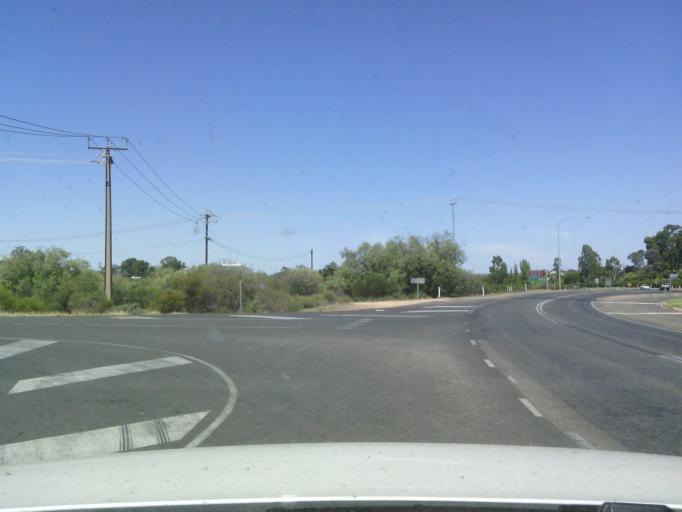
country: AU
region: South Australia
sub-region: Berri and Barmera
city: Monash
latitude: -34.2794
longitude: 140.5470
